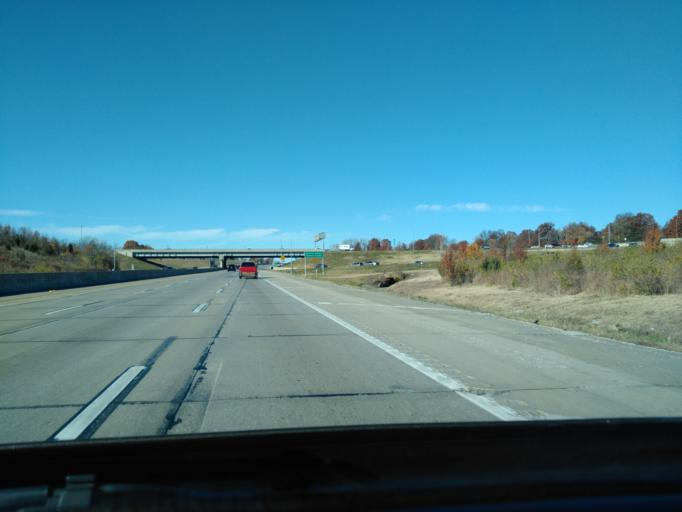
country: US
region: Missouri
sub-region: Saint Louis County
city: Oakville
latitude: 38.4939
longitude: -90.2991
